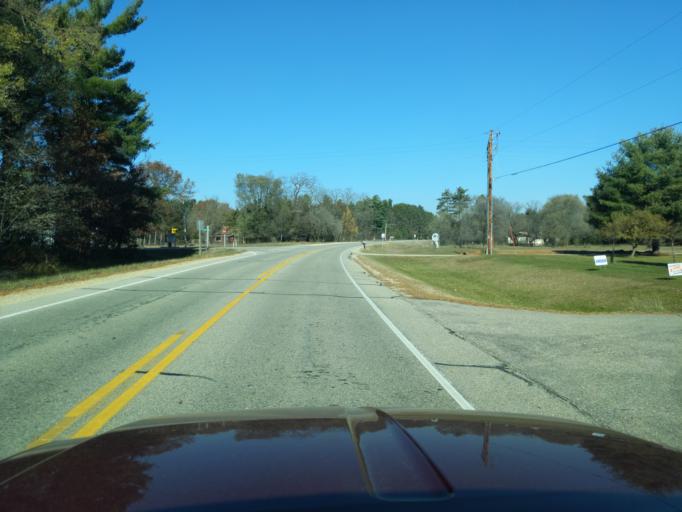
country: US
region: Wisconsin
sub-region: Waushara County
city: Wautoma
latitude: 44.0619
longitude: -89.2969
